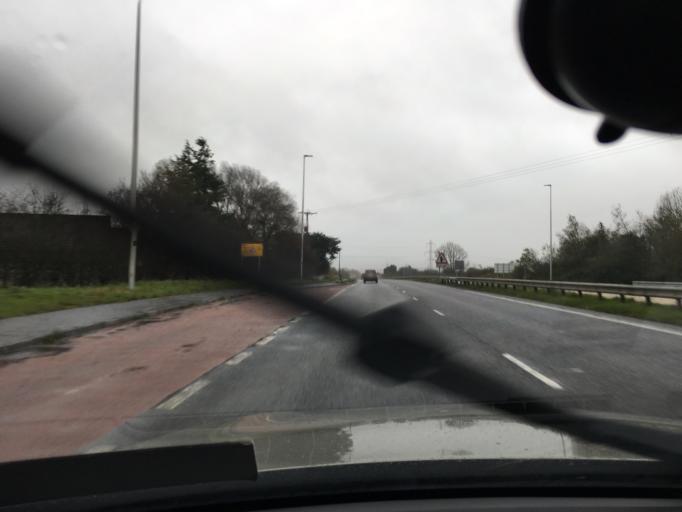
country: GB
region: Northern Ireland
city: Carnmoney
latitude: 54.7245
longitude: -5.9689
